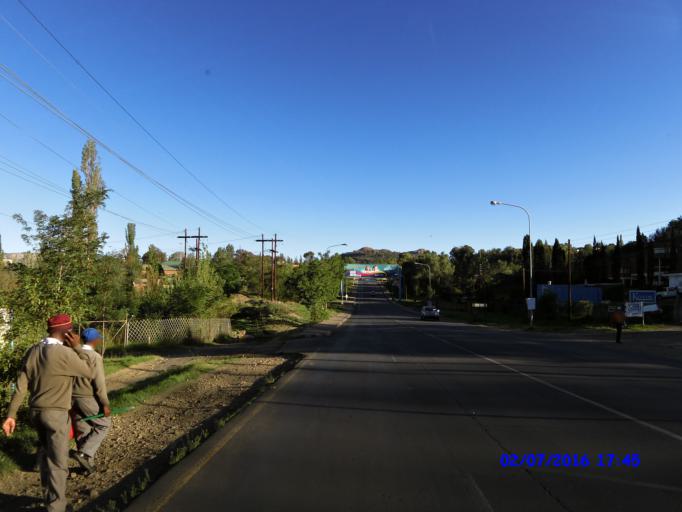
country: LS
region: Maseru
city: Maseru
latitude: -29.3008
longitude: 27.4815
